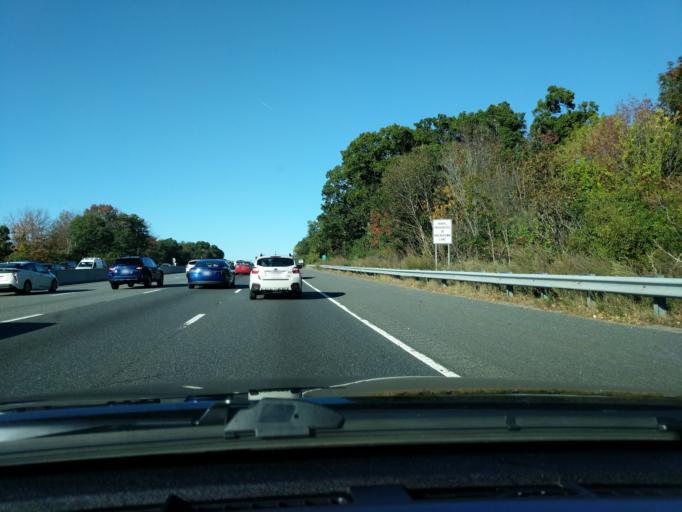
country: US
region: Massachusetts
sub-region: Middlesex County
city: Waltham
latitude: 42.4094
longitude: -71.2582
